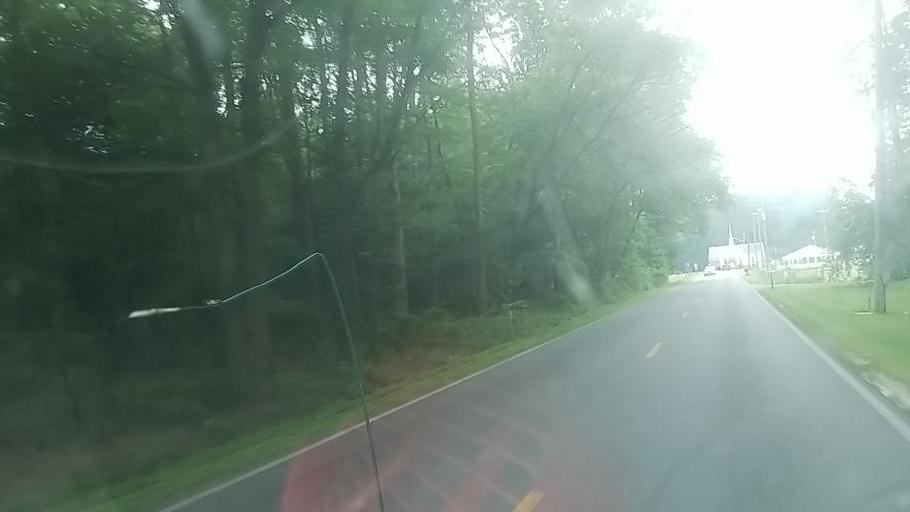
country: US
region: Maryland
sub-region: Wicomico County
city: Delmar
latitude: 38.3982
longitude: -75.5328
